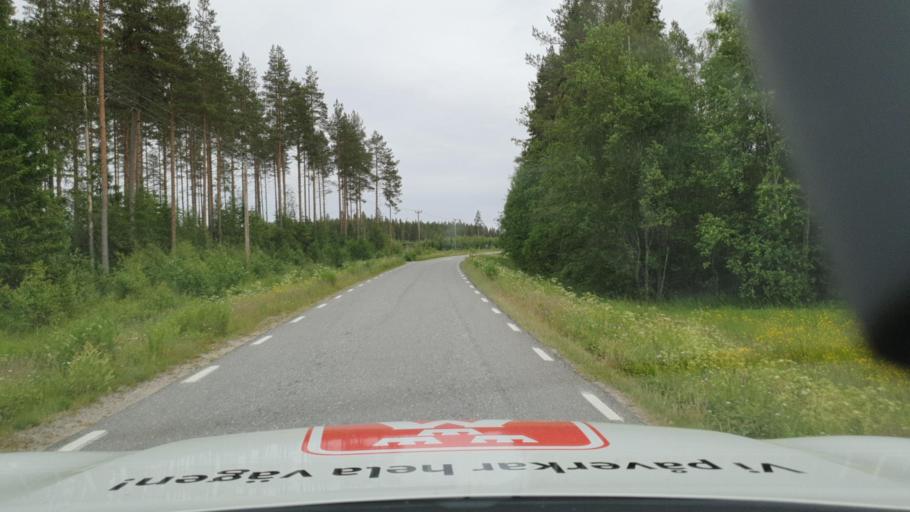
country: SE
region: Vaesterbotten
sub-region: Nordmalings Kommun
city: Nordmaling
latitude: 63.5201
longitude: 19.4201
